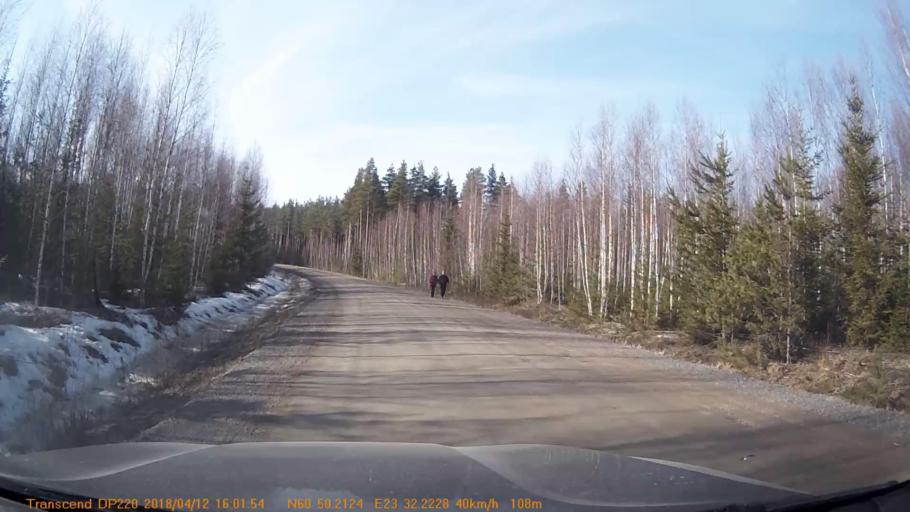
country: FI
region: Haeme
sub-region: Forssa
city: Jokioinen
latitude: 60.8372
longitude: 23.5364
